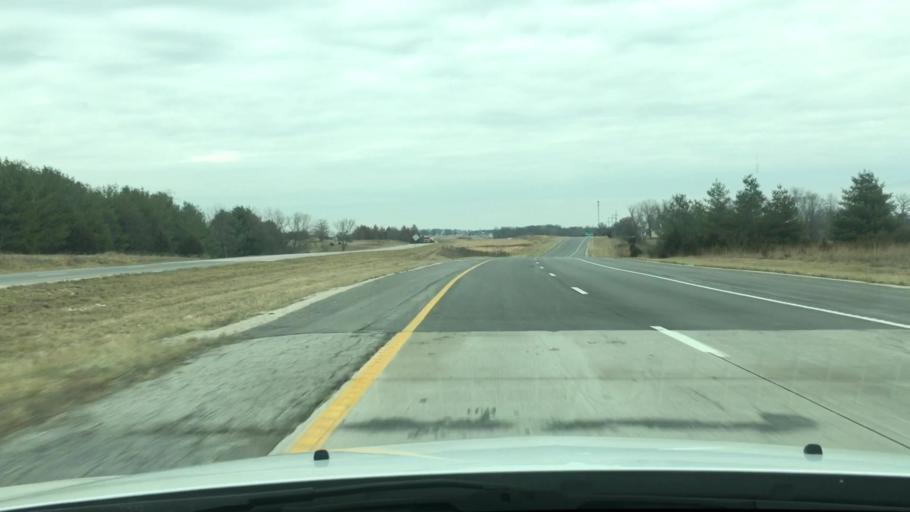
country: US
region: Missouri
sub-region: Audrain County
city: Mexico
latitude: 39.0954
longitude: -91.8987
